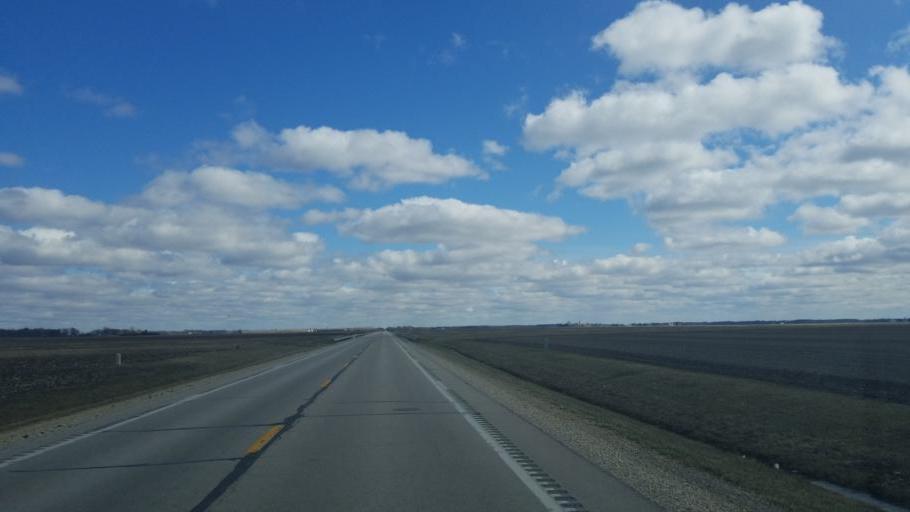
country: US
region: Illinois
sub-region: Douglas County
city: Villa Grove
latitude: 39.7920
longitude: -88.0998
